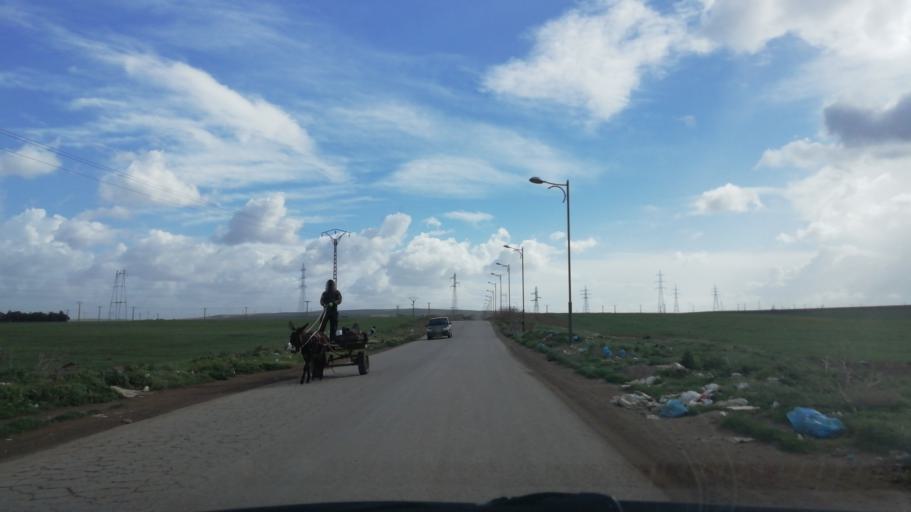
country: DZ
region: Oran
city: Sidi ech Chahmi
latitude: 35.6370
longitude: -0.5474
